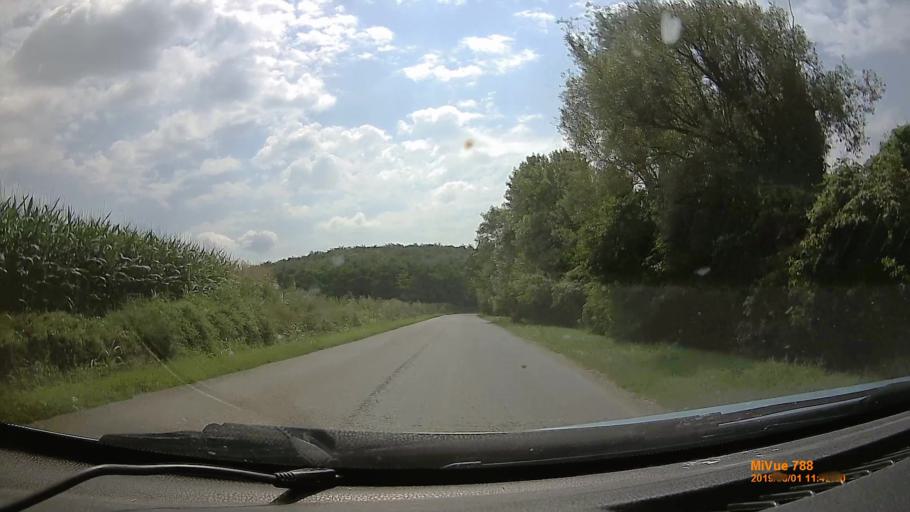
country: HU
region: Baranya
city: Villany
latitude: 45.8888
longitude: 18.4104
